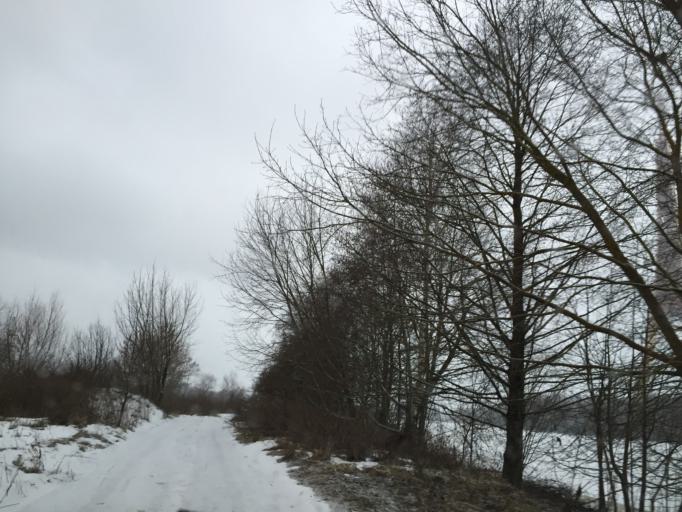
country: LV
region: Riga
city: Riga
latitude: 56.9195
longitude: 24.1386
